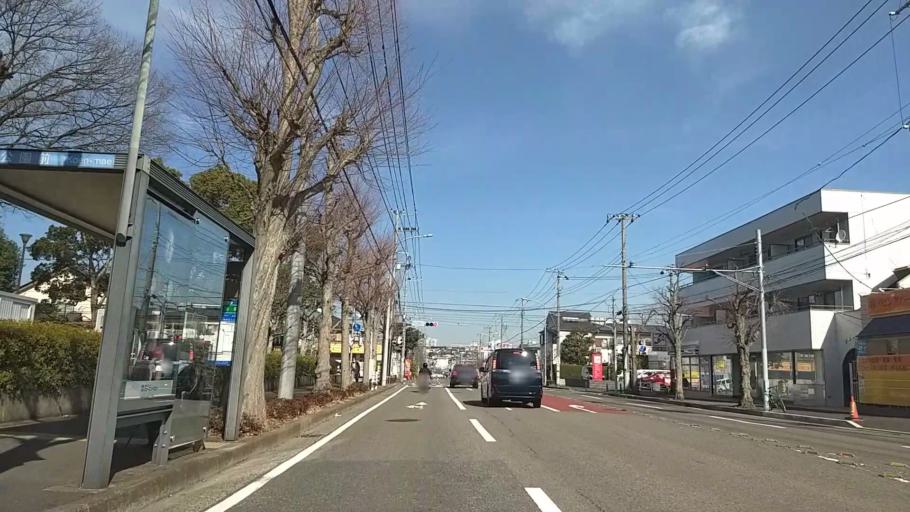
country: JP
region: Kanagawa
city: Kamakura
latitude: 35.3767
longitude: 139.5811
